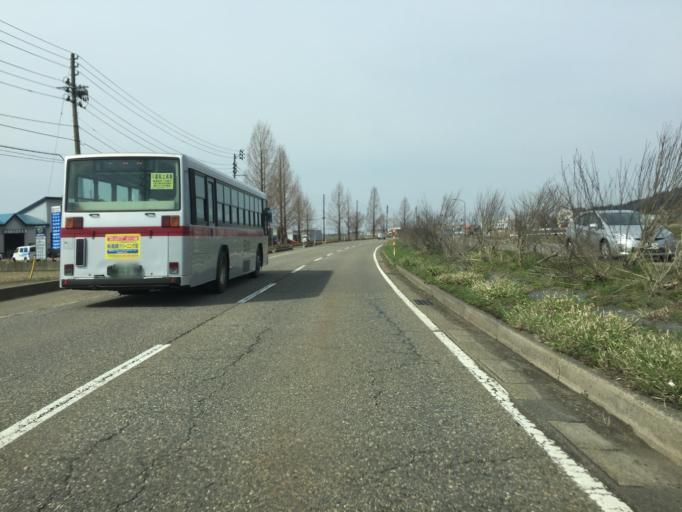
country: JP
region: Niigata
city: Ojiya
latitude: 37.3546
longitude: 138.8291
